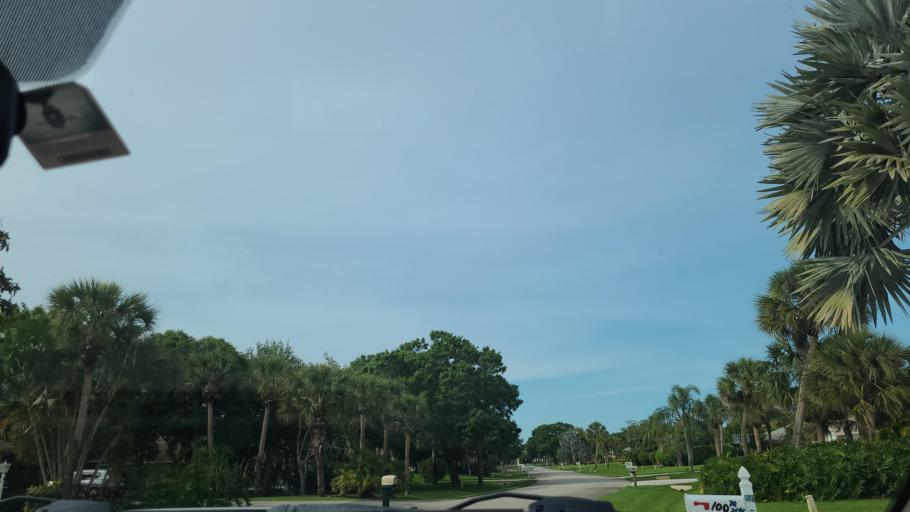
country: US
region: Florida
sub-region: Indian River County
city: Sebastian
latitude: 27.7894
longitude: -80.4793
